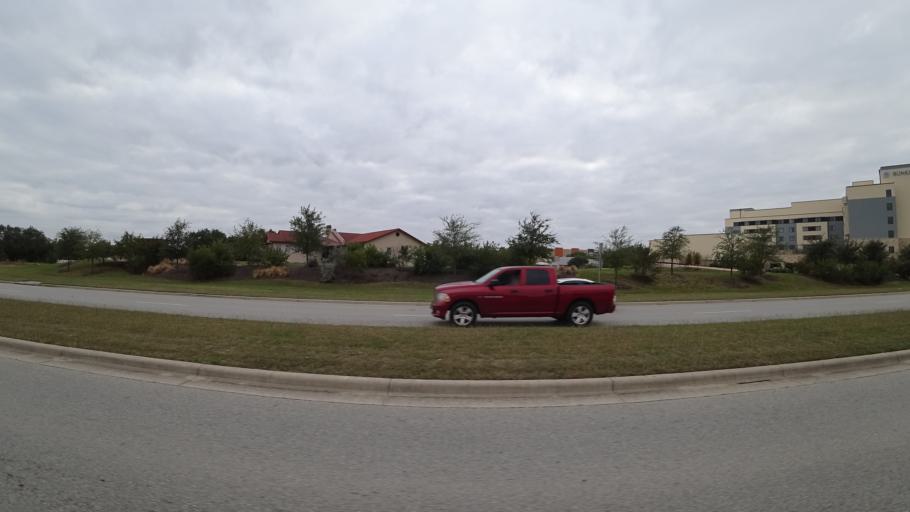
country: US
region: Texas
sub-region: Travis County
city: Bee Cave
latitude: 30.3096
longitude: -97.9339
